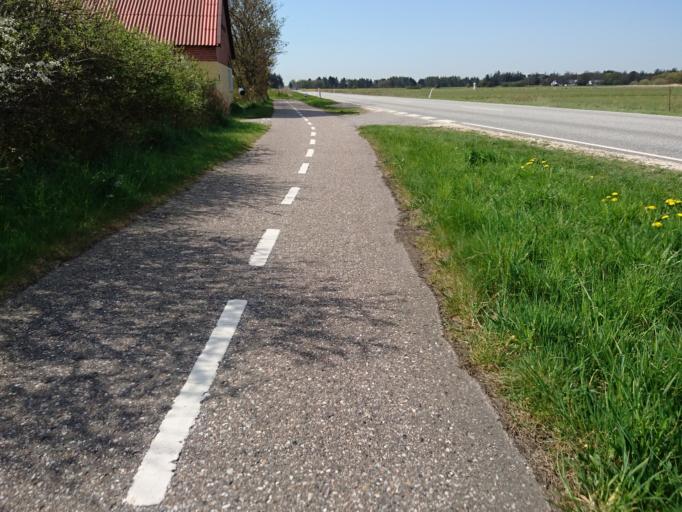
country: DK
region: North Denmark
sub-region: Frederikshavn Kommune
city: Strandby
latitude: 57.6264
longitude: 10.4449
